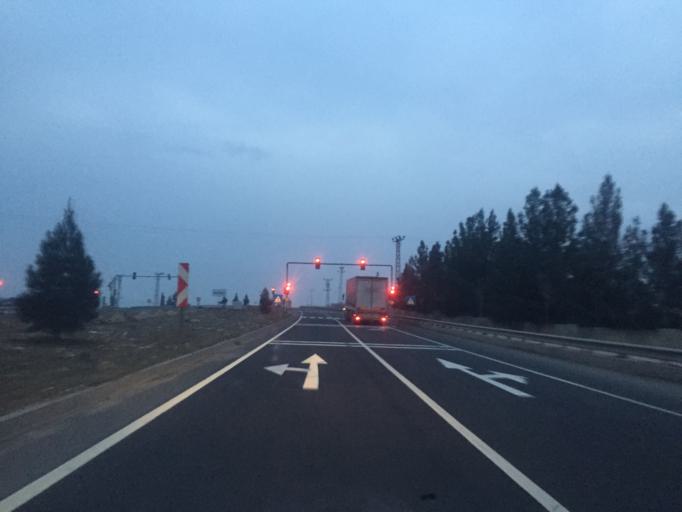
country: TR
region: Sanliurfa
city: Camlidere
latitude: 37.1534
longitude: 39.0680
